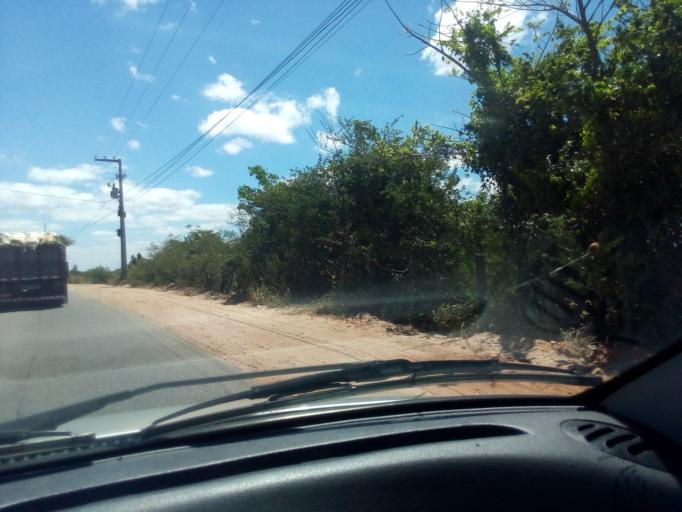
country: BR
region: Rio Grande do Norte
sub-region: Sao Goncalo Do Amarante
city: Sao Goncalo do Amarante
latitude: -5.7984
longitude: -35.3294
